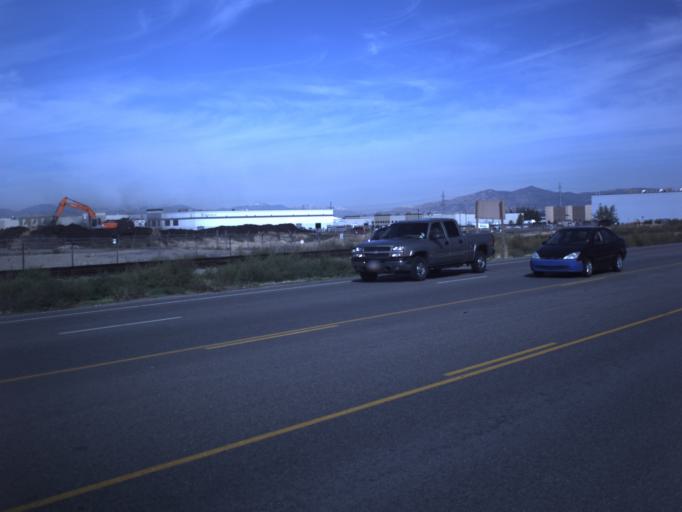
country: US
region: Utah
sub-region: Utah County
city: Lindon
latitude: 40.3246
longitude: -111.7369
